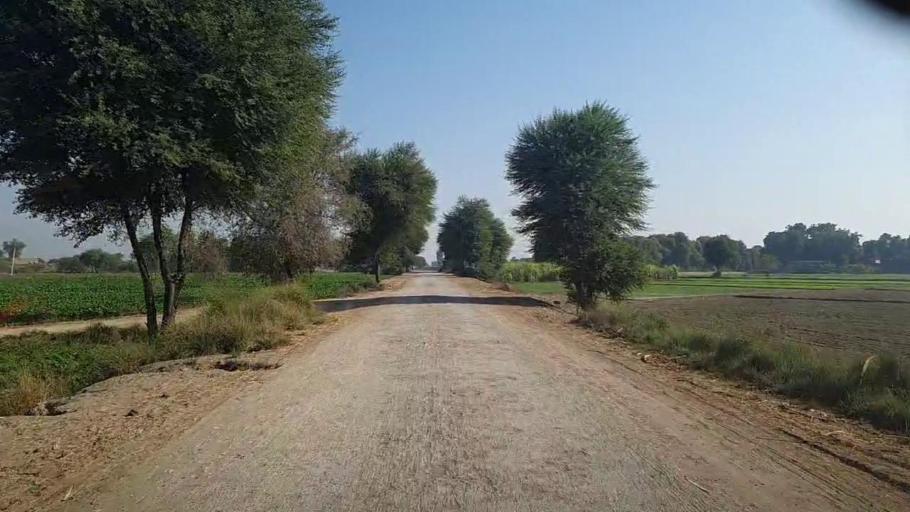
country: PK
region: Sindh
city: Darya Khan Marri
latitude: 26.6599
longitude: 68.3441
